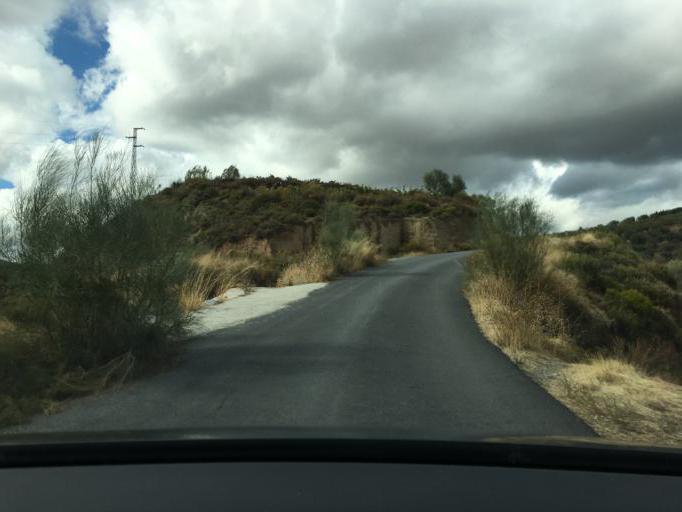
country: ES
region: Andalusia
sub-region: Provincia de Granada
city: Quentar
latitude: 37.2000
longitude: -3.4698
